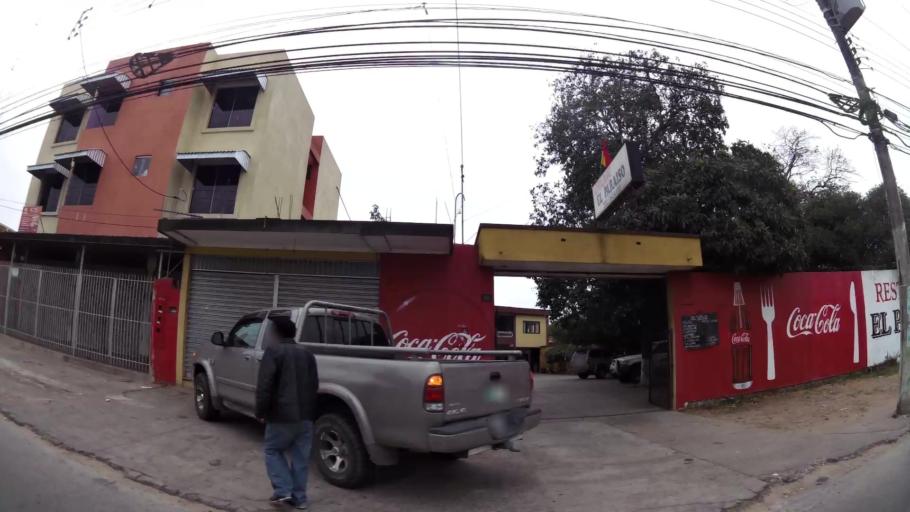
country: BO
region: Santa Cruz
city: Santa Cruz de la Sierra
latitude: -17.7748
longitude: -63.2052
